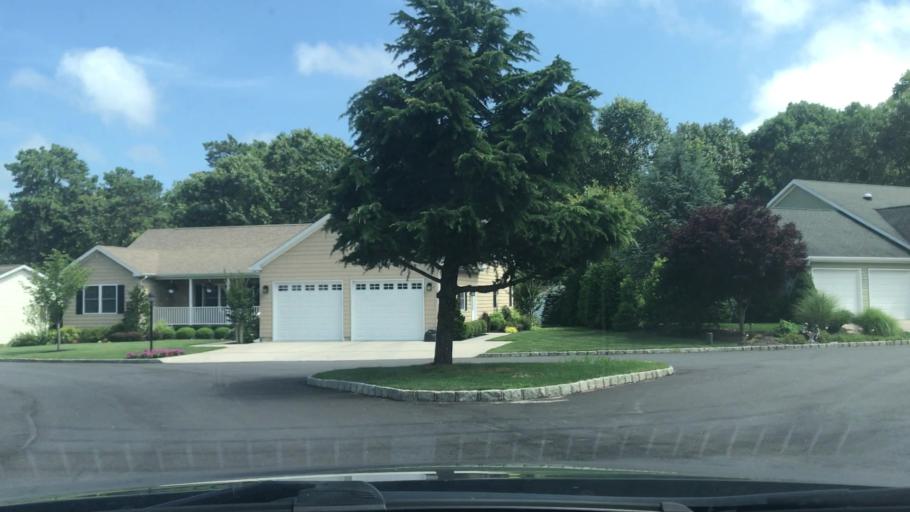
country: US
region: New York
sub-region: Suffolk County
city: Calverton
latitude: 40.9304
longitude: -72.7060
